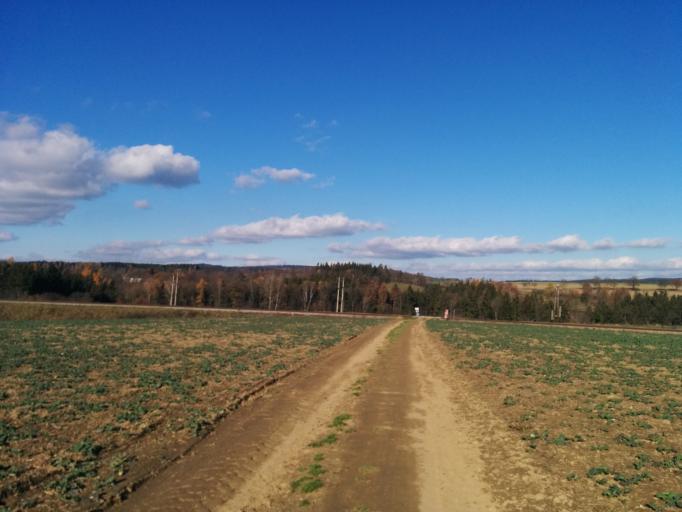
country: CZ
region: Vysocina
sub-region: Okres Jihlava
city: Jihlava
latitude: 49.4132
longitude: 15.5442
